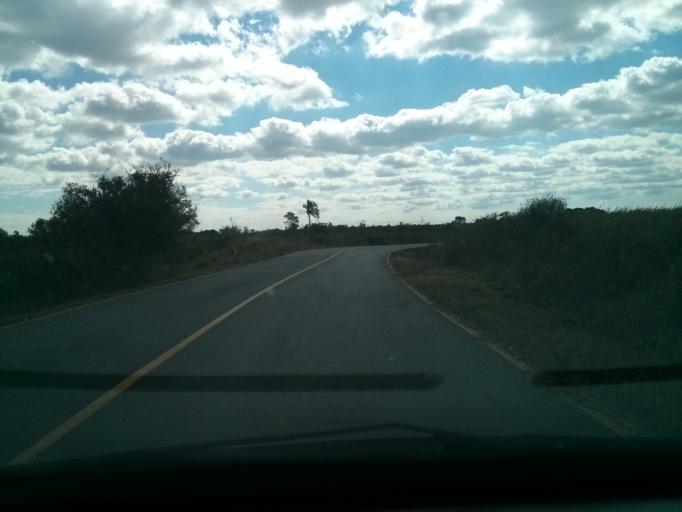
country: BR
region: Parana
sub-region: Sao Jose Dos Pinhais
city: Sao Jose dos Pinhais
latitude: -25.5325
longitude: -49.2256
